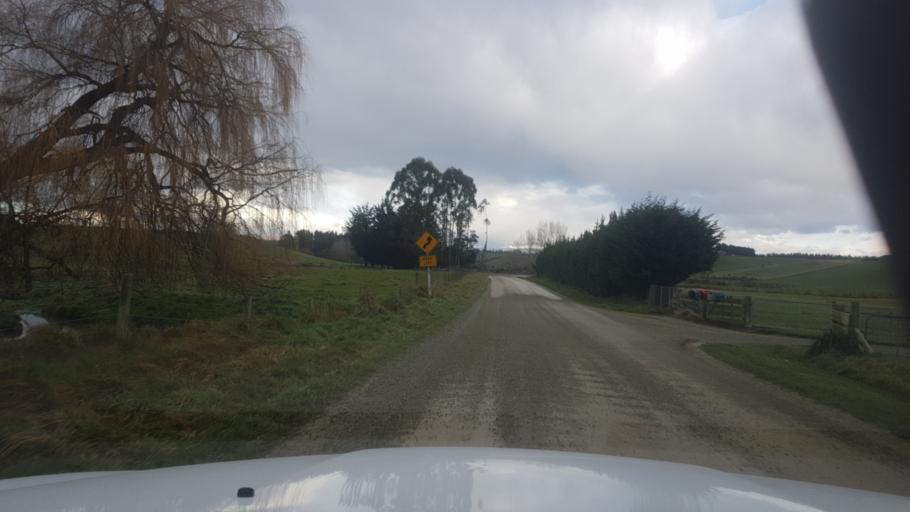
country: NZ
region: Canterbury
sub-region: Timaru District
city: Pleasant Point
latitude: -44.3378
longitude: 171.1826
